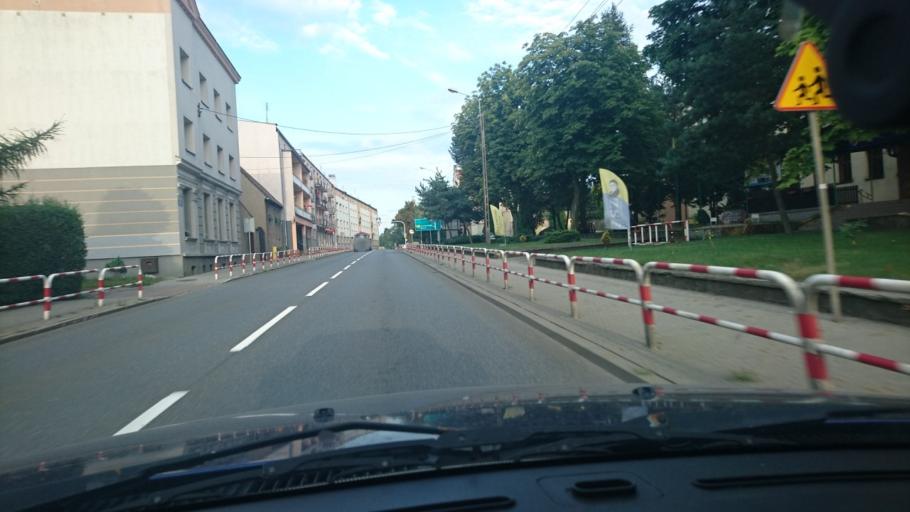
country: PL
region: Opole Voivodeship
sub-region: Powiat oleski
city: Olesno
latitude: 50.8746
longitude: 18.4221
